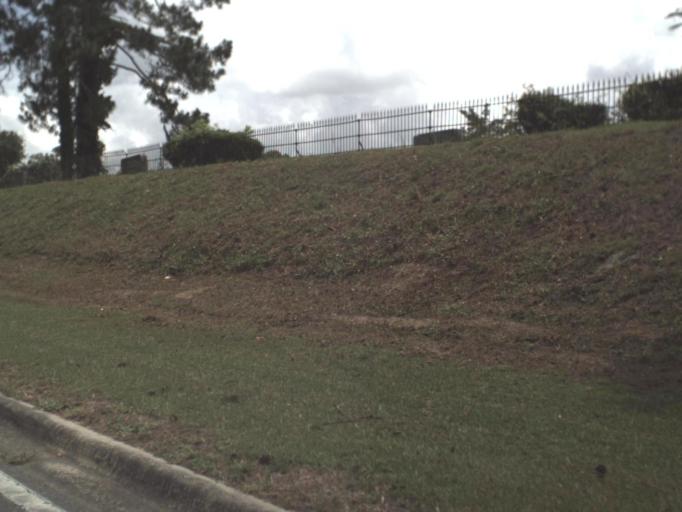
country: US
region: Florida
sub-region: Madison County
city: Madison
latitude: 30.4763
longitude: -83.4159
